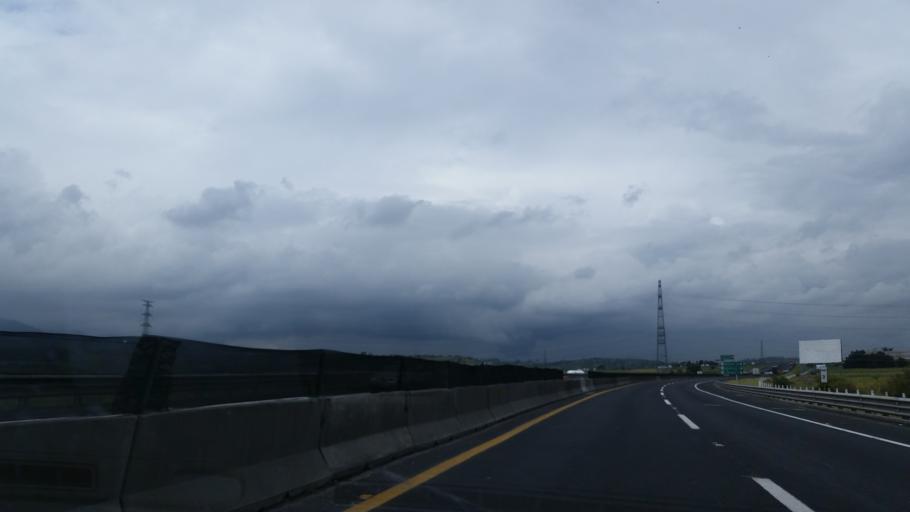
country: MX
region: Mexico
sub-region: Huehuetoca
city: Casa Nueva
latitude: 19.8237
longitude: -99.2246
